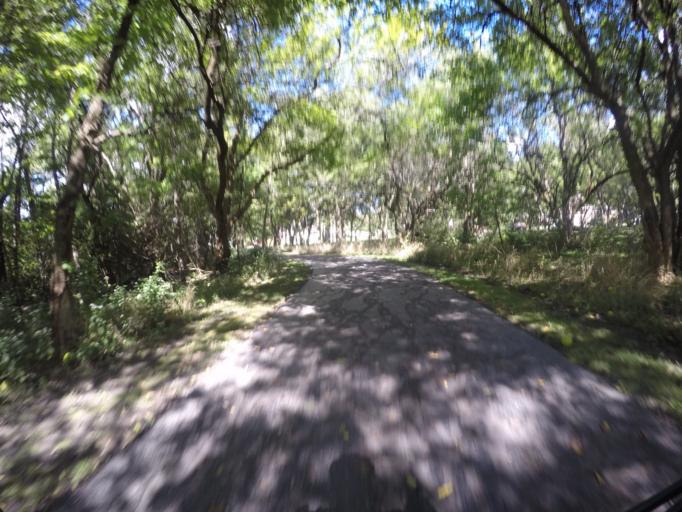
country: US
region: Kansas
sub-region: Johnson County
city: Olathe
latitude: 38.8491
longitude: -94.7905
